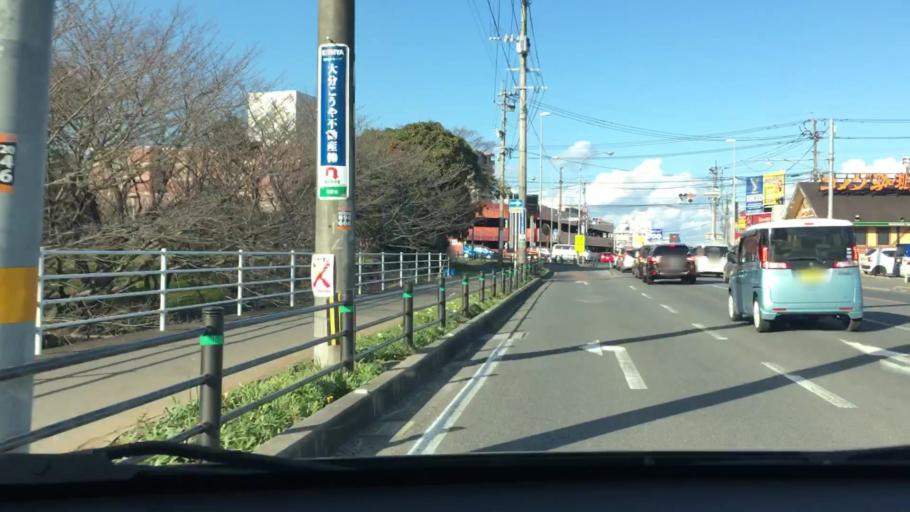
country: JP
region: Oita
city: Tsurusaki
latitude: 33.2243
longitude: 131.6592
